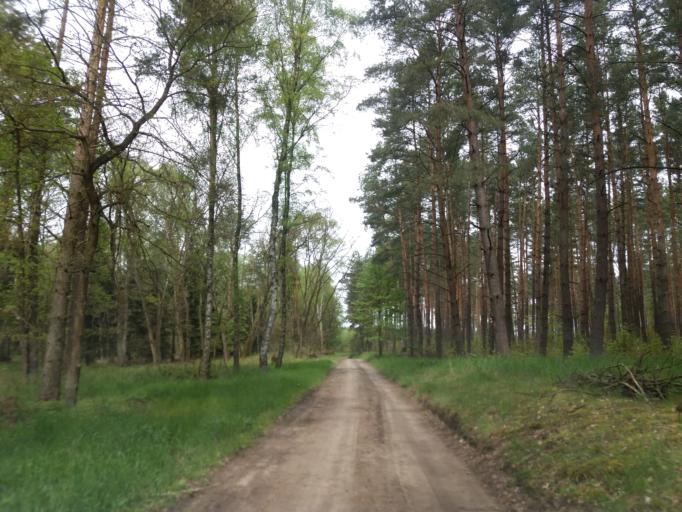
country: PL
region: Lubusz
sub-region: Powiat strzelecko-drezdenecki
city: Dobiegniew
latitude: 53.0004
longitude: 15.7202
